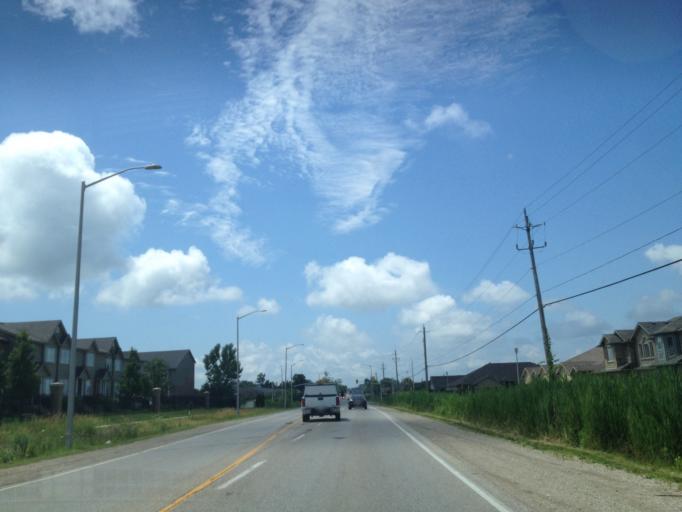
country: CA
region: Ontario
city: London
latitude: 43.0022
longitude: -81.3202
